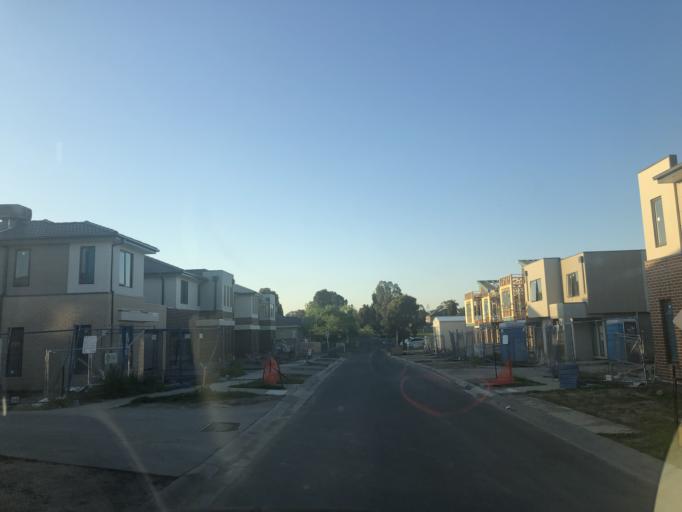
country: AU
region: Victoria
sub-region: Casey
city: Lynbrook
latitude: -38.0464
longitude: 145.2604
